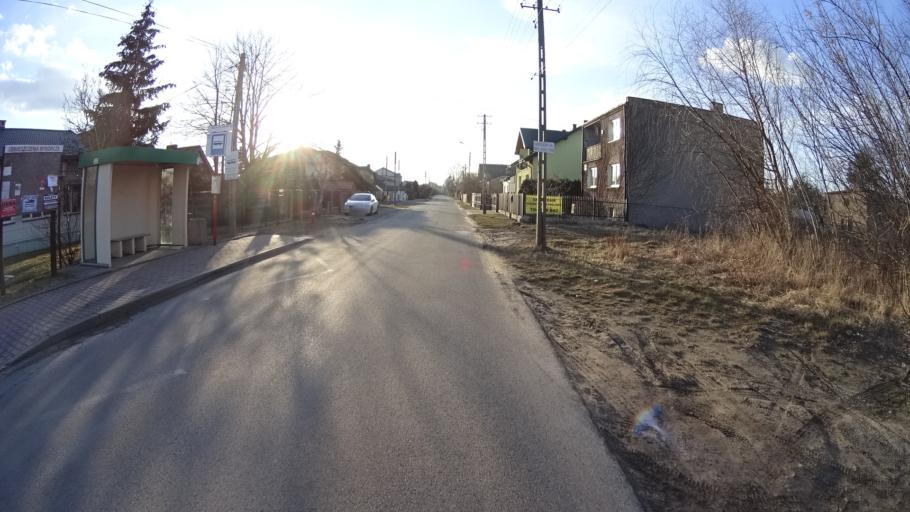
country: PL
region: Masovian Voivodeship
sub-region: Powiat warszawski zachodni
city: Truskaw
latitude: 52.2592
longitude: 20.7657
